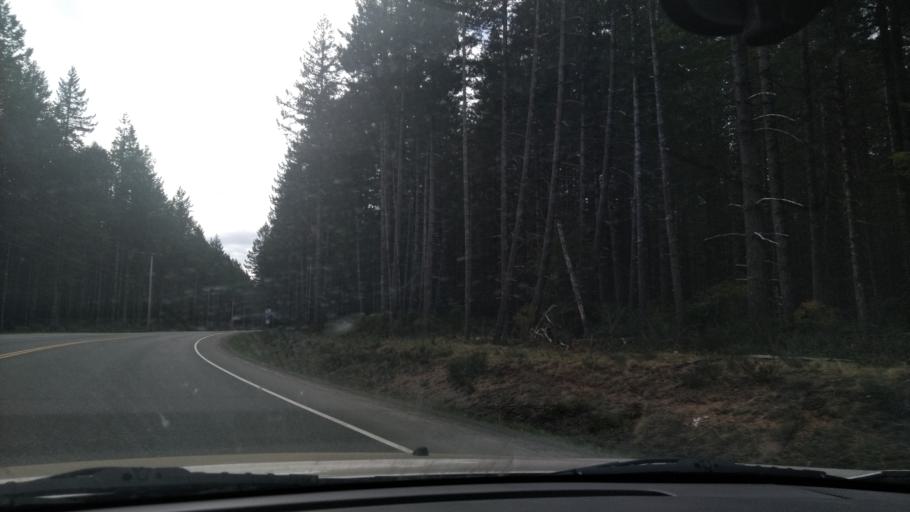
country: CA
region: British Columbia
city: Campbell River
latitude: 50.0351
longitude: -125.3316
